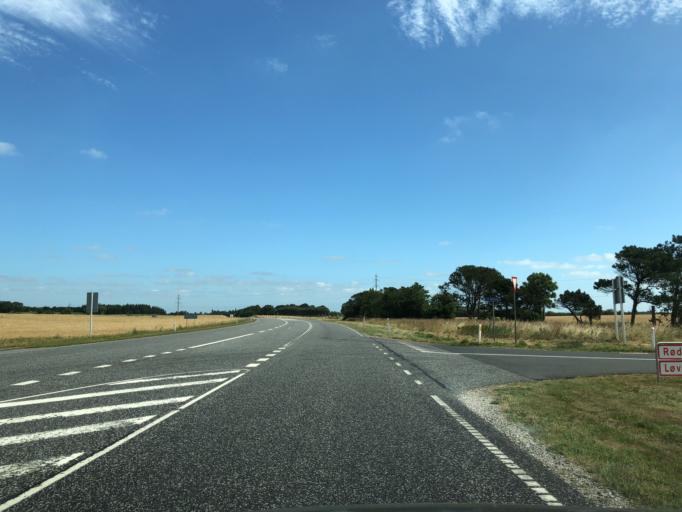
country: DK
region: Central Jutland
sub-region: Viborg Kommune
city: Viborg
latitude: 56.5417
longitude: 9.4729
